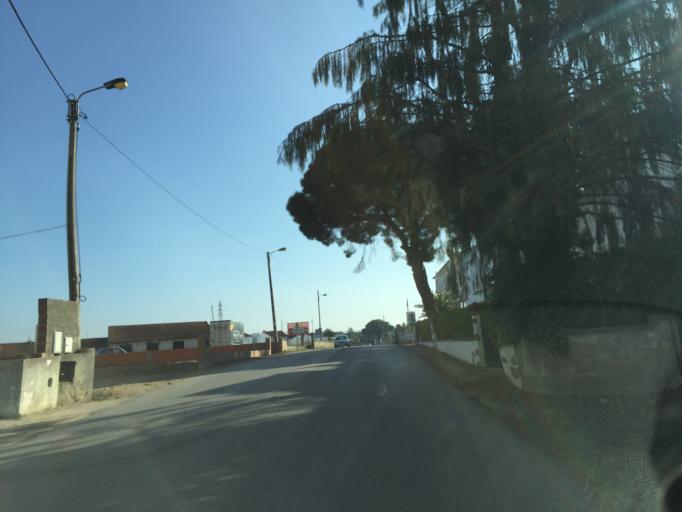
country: PT
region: Santarem
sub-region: Abrantes
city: Abrantes
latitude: 39.4796
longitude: -8.1893
